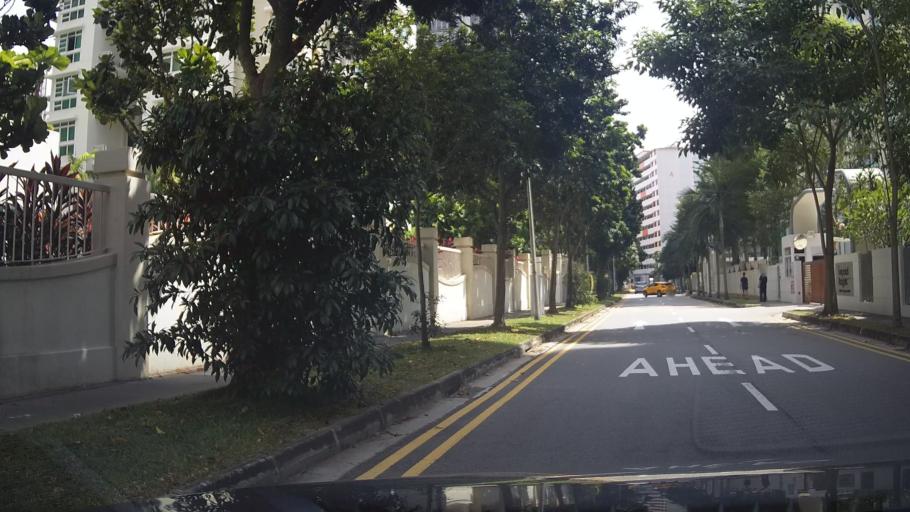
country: SG
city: Singapore
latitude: 1.3117
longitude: 103.8949
